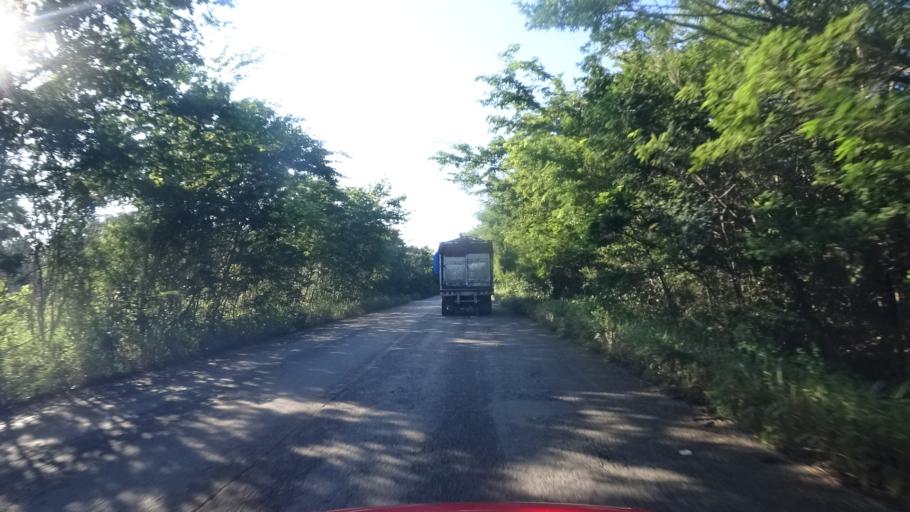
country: MX
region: Yucatan
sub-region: Tizimin
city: Tizimin
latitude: 21.1116
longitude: -88.1811
